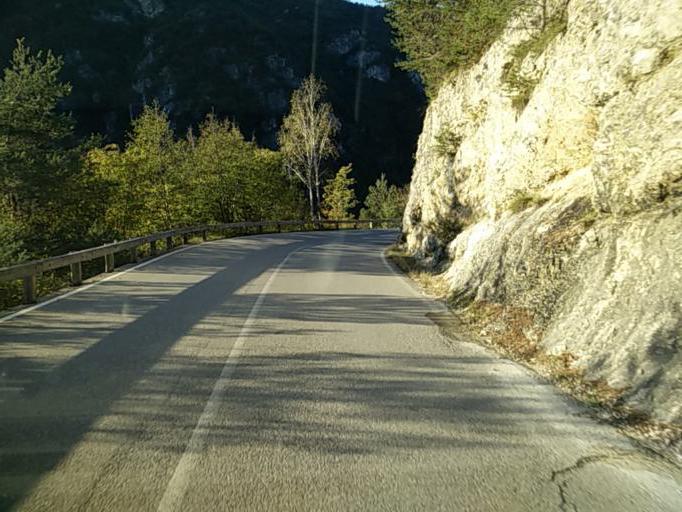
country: IT
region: Lombardy
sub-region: Provincia di Brescia
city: Gargnano
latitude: 45.6926
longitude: 10.6108
